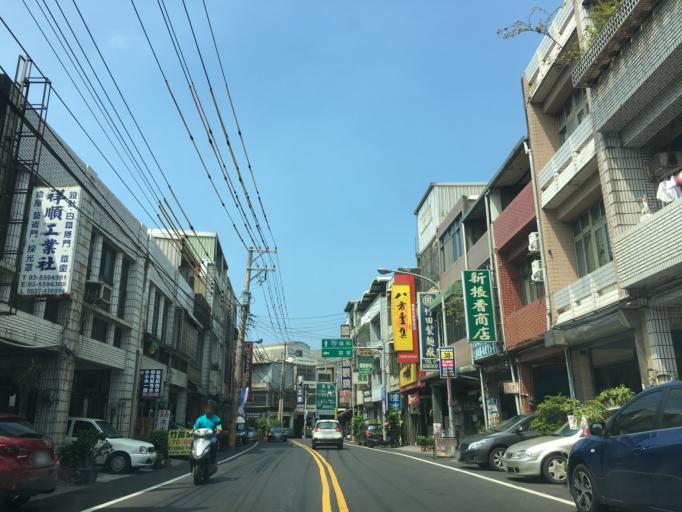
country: TW
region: Taiwan
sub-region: Hsinchu
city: Zhubei
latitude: 24.9027
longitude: 120.9863
